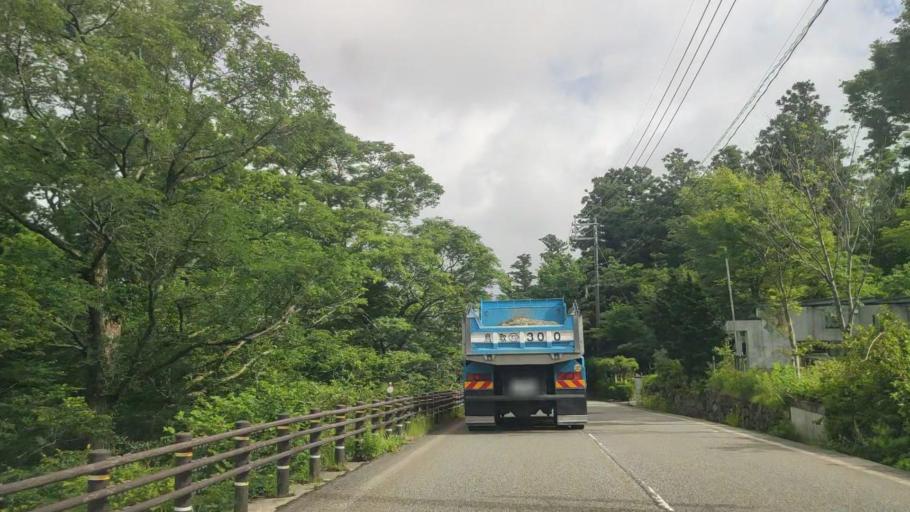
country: JP
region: Tottori
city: Yonago
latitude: 35.3920
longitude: 133.5308
